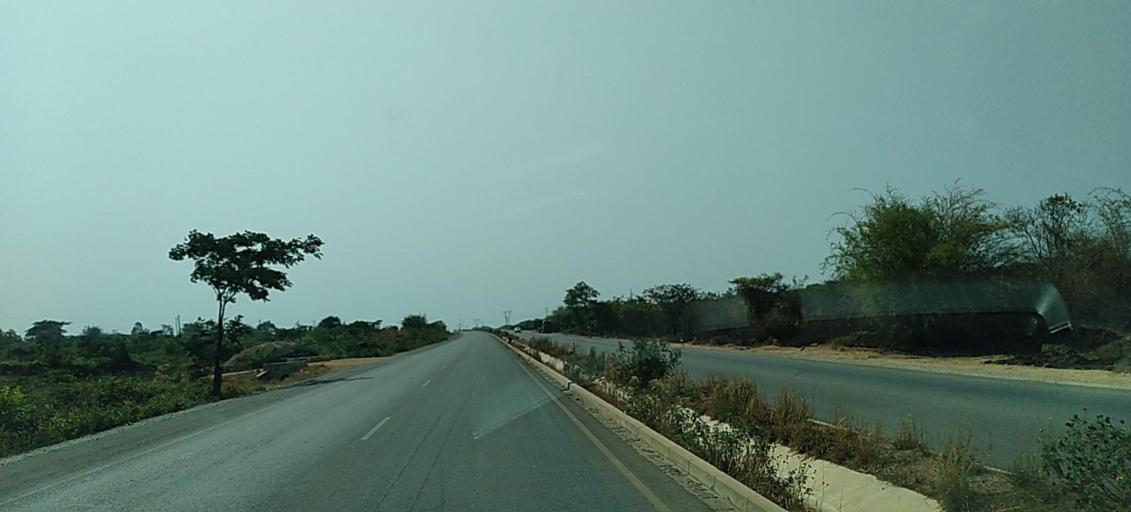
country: ZM
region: Copperbelt
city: Chingola
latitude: -12.5804
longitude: 27.9268
